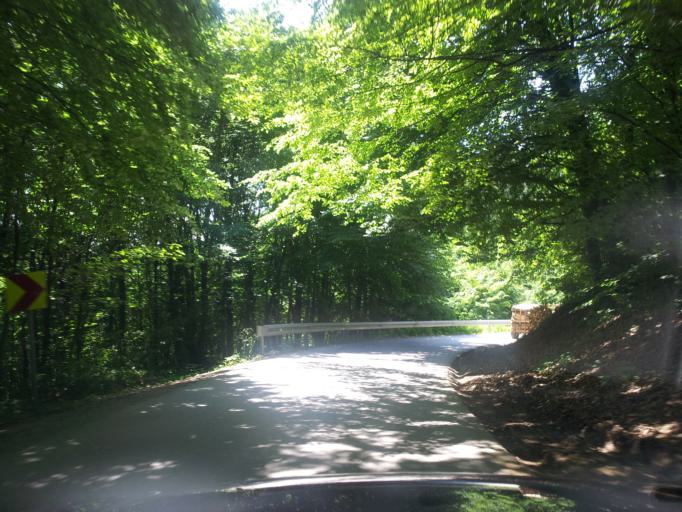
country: HR
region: Karlovacka
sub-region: Grad Karlovac
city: Karlovac
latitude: 45.4703
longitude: 15.4777
